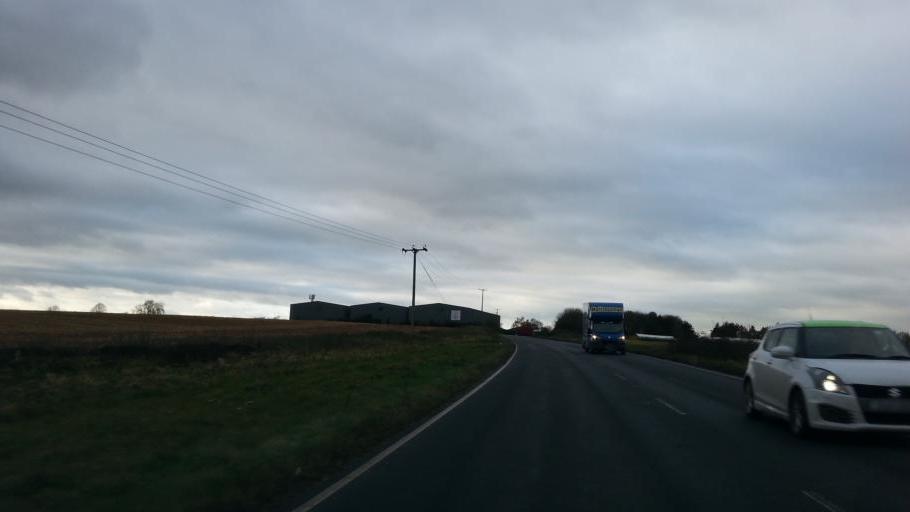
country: GB
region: England
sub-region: Norfolk
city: Feltwell
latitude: 52.5593
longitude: 0.5449
